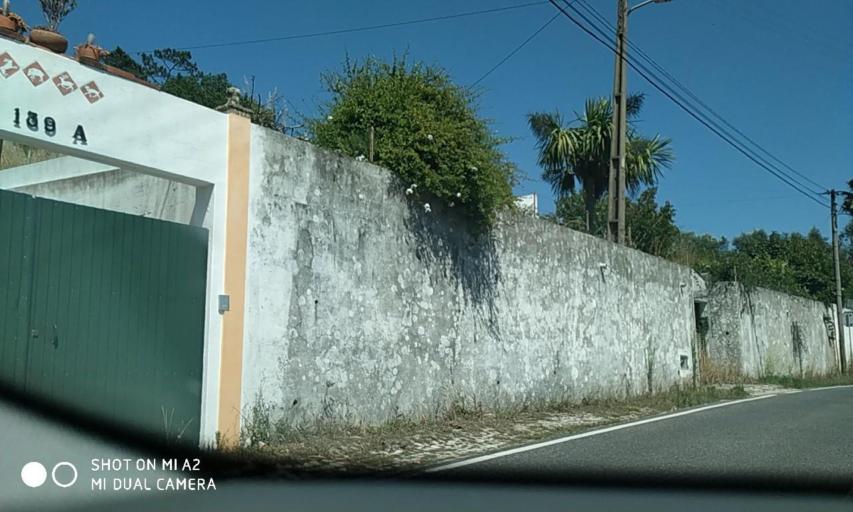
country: PT
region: Lisbon
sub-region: Sintra
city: Almargem
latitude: 38.8245
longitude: -9.2723
